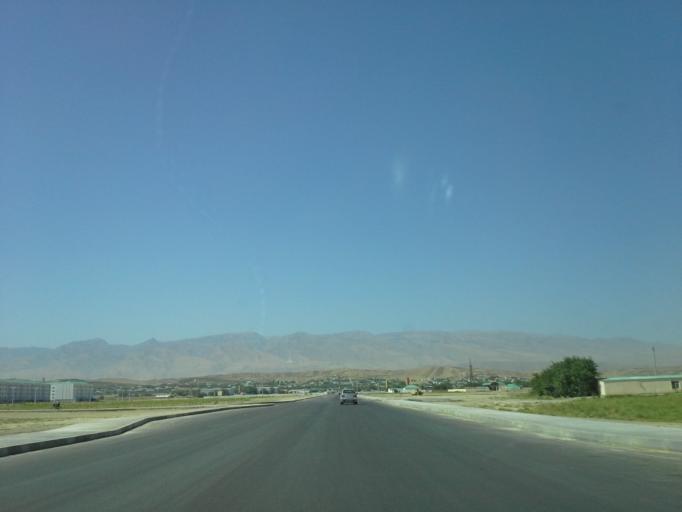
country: TM
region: Ahal
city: Ashgabat
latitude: 37.9820
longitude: 58.3236
